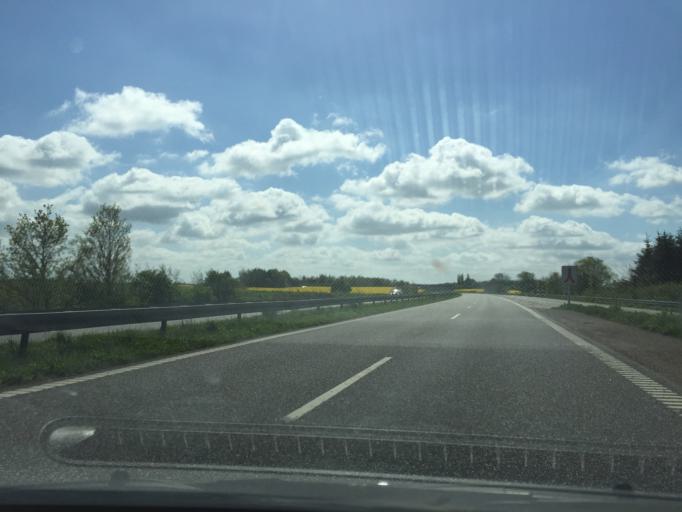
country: DK
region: Zealand
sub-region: Guldborgsund Kommune
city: Norre Alslev
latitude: 54.8612
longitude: 11.8497
